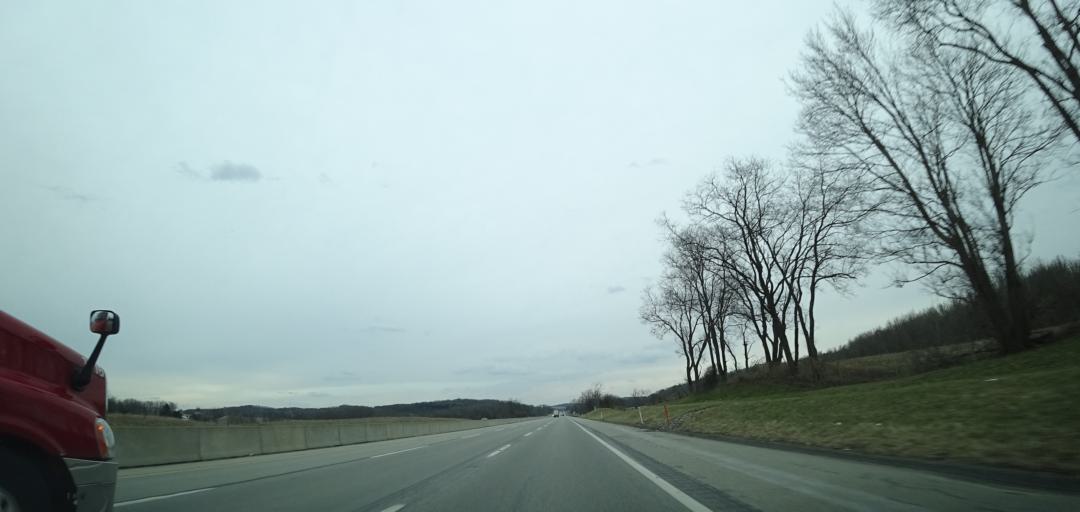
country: US
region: Pennsylvania
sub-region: Lawrence County
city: New Beaver
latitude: 40.8840
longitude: -80.4274
